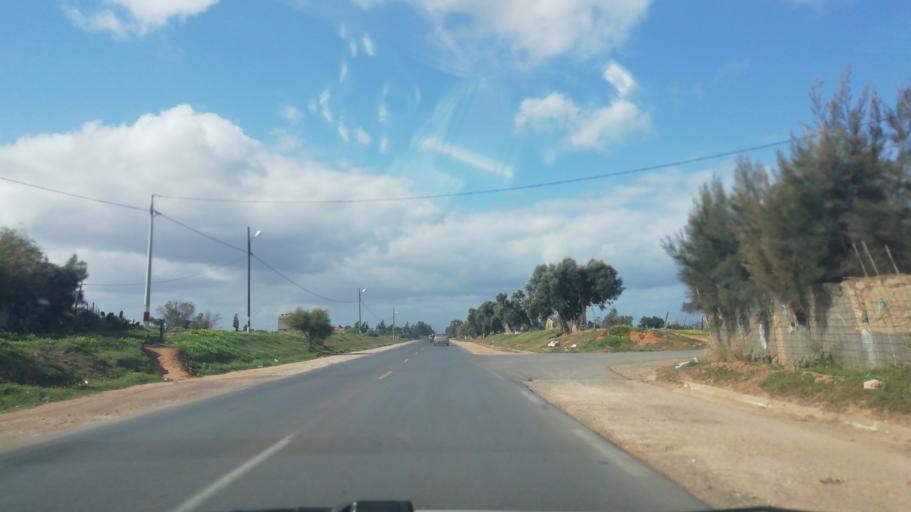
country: DZ
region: Relizane
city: Mazouna
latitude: 36.2578
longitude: 0.5943
